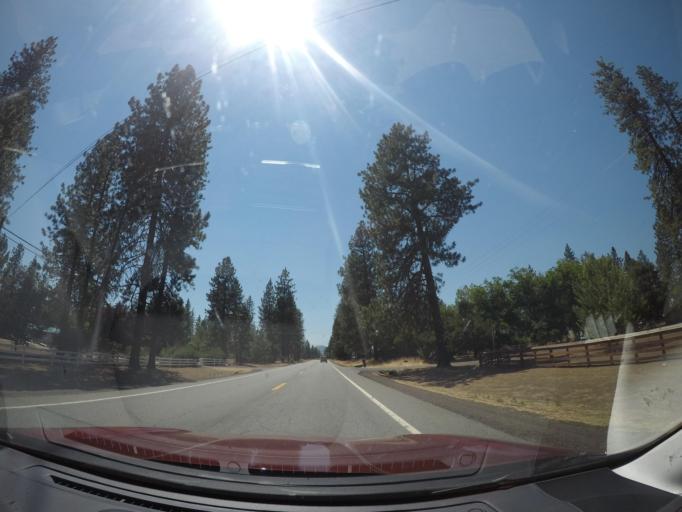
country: US
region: California
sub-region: Shasta County
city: Burney
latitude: 41.0608
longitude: -121.3699
